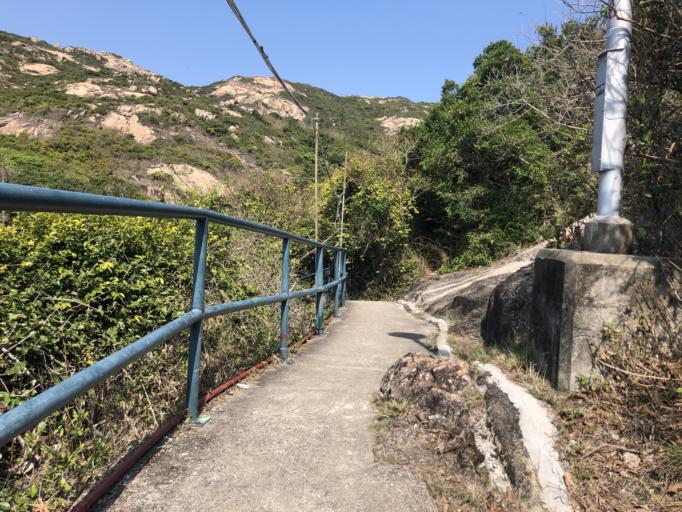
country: HK
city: Sok Kwu Wan
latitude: 22.1643
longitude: 114.2542
